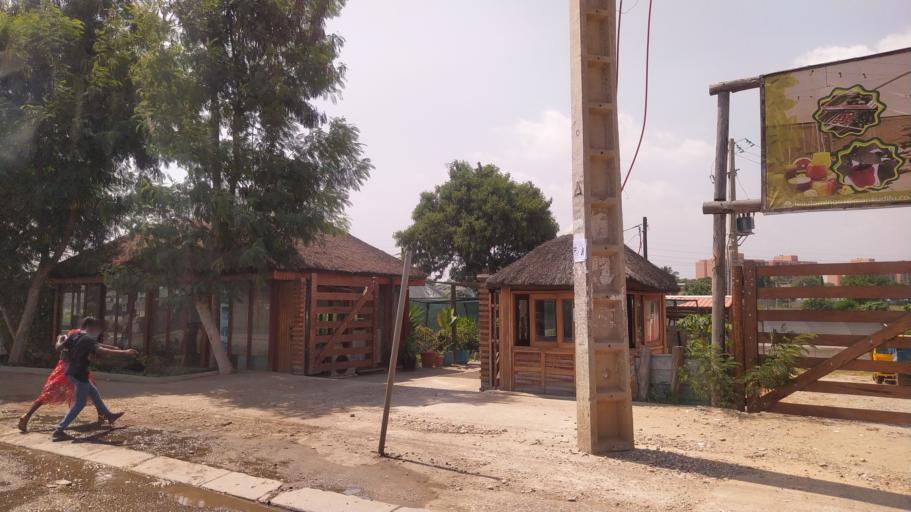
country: AO
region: Luanda
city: Luanda
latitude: -8.9022
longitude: 13.2330
